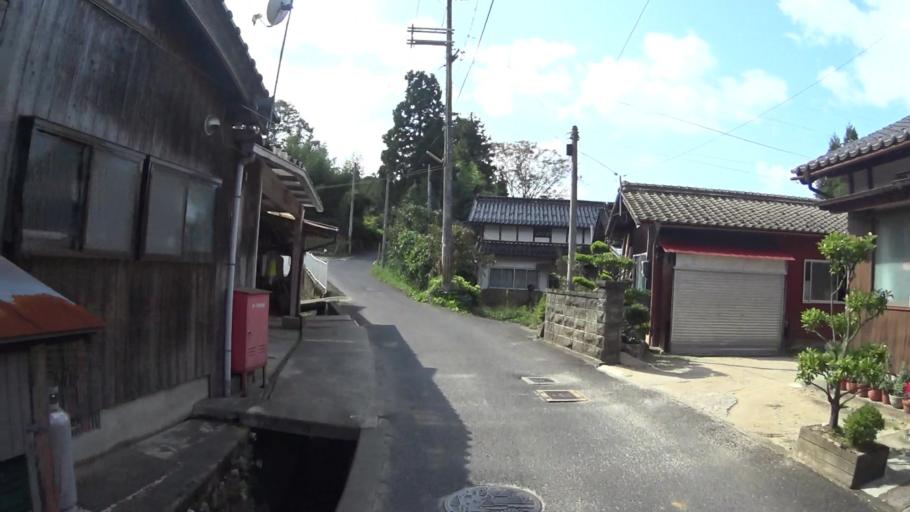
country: JP
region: Kyoto
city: Miyazu
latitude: 35.6568
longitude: 135.1107
